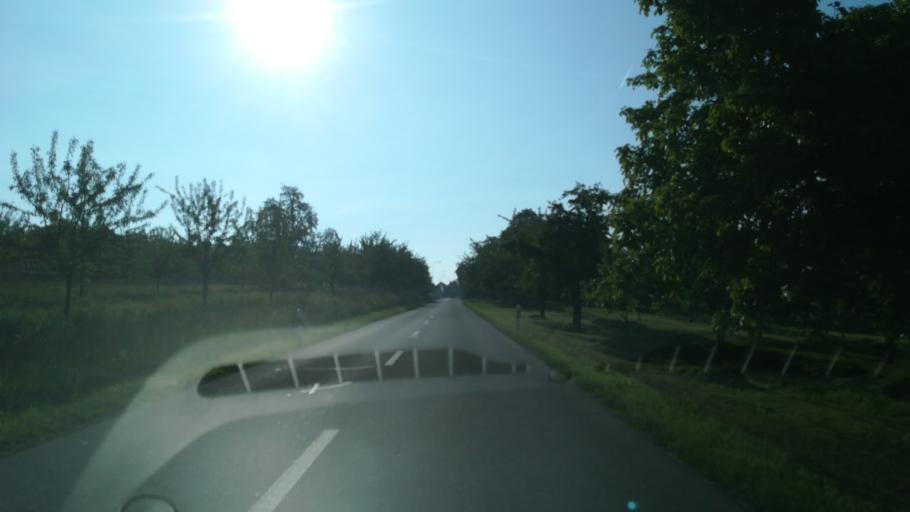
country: CH
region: Thurgau
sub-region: Frauenfeld District
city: Homburg
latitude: 47.6349
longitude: 8.9997
